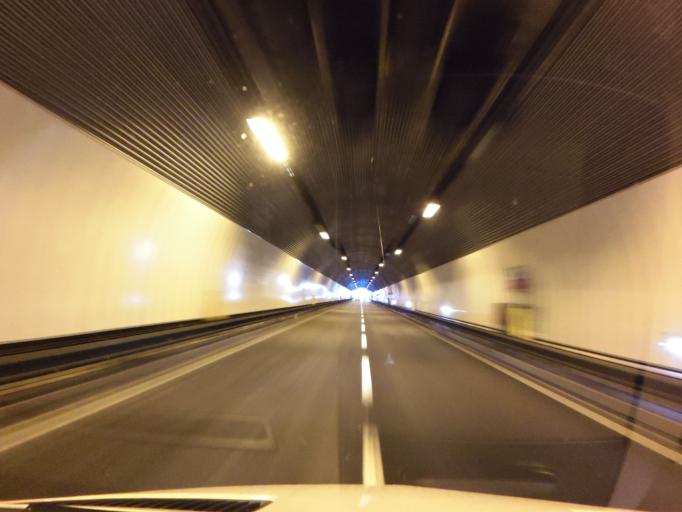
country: IT
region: Trentino-Alto Adige
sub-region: Provincia di Trento
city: Trento
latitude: 46.0688
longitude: 11.1088
